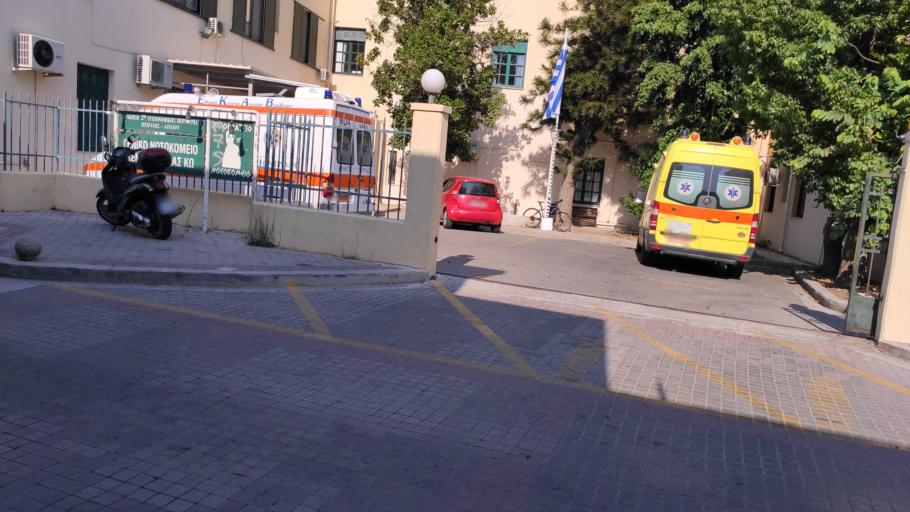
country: GR
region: South Aegean
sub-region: Nomos Dodekanisou
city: Kos
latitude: 36.8924
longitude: 27.2911
